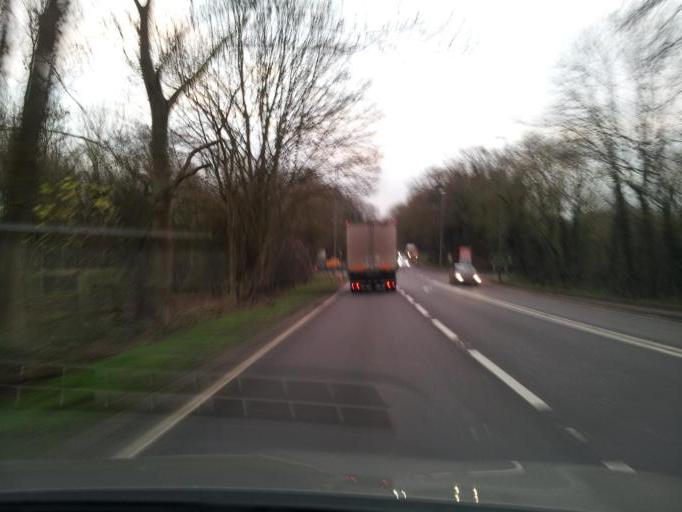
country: GB
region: England
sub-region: Cambridgeshire
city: Girton
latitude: 52.2146
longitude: 0.0656
